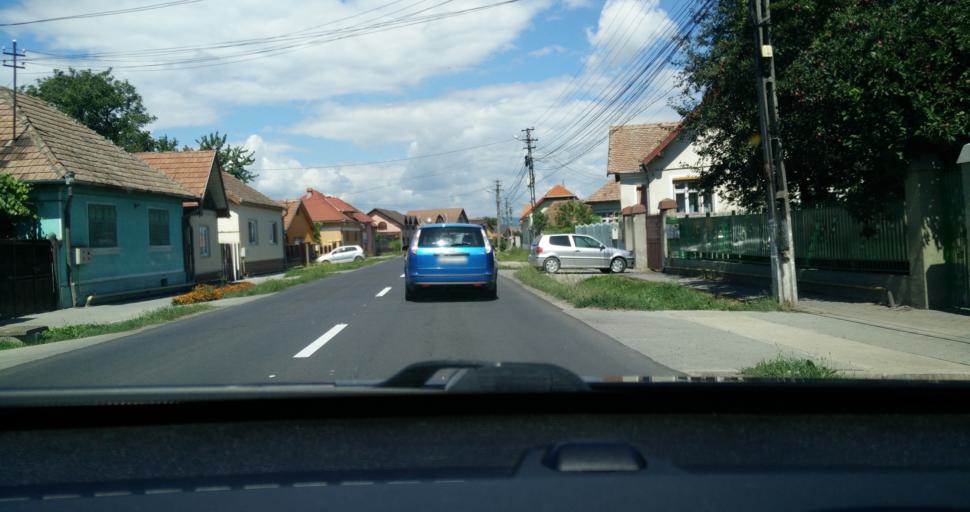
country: RO
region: Alba
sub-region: Municipiul Sebes
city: Petresti
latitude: 45.9257
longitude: 23.5616
